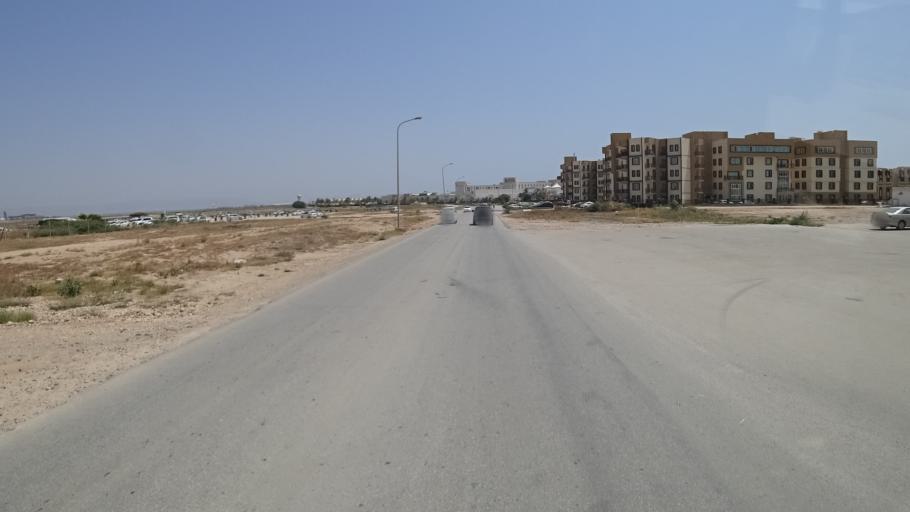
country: OM
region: Zufar
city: Salalah
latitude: 17.0242
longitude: 54.0594
